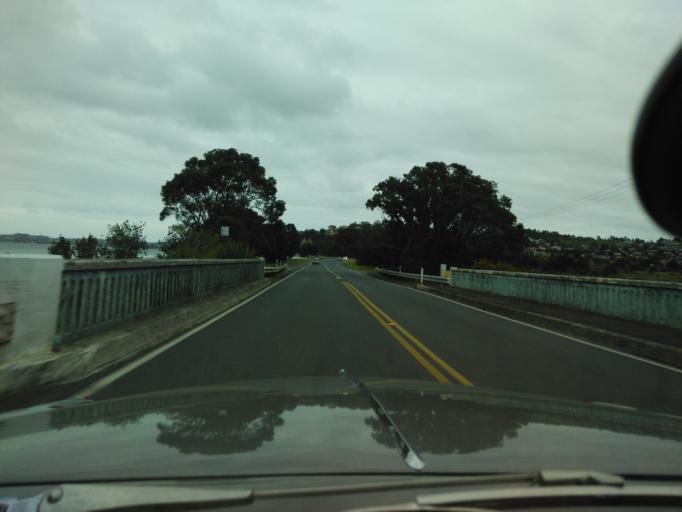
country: NZ
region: Auckland
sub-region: Auckland
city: Warkworth
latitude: -36.5613
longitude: 174.6966
